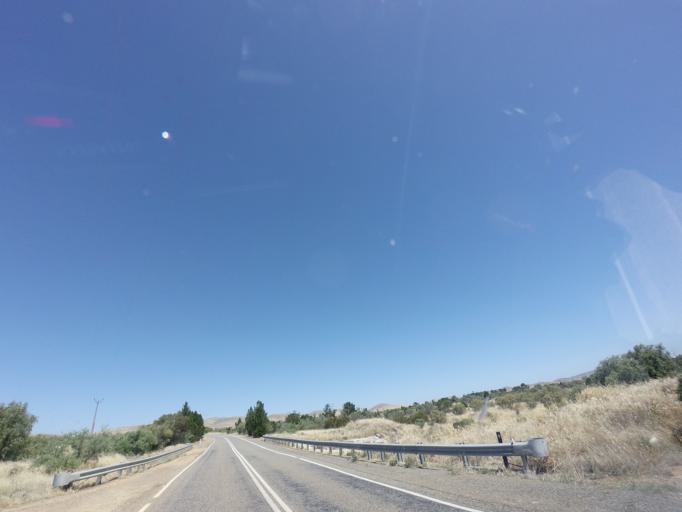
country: AU
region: South Australia
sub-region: Peterborough
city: Peterborough
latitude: -32.7221
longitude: 138.4962
